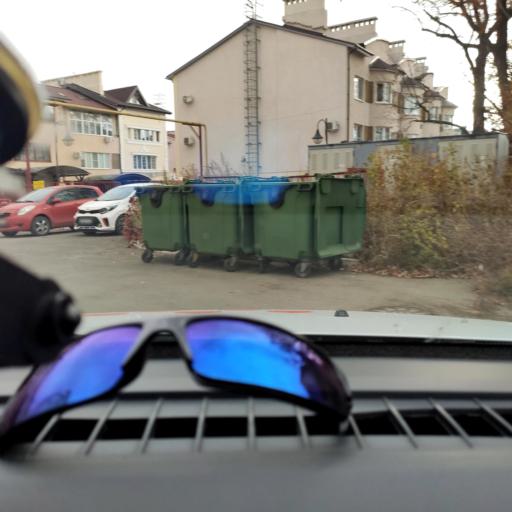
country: RU
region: Samara
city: Samara
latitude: 53.2362
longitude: 50.1727
